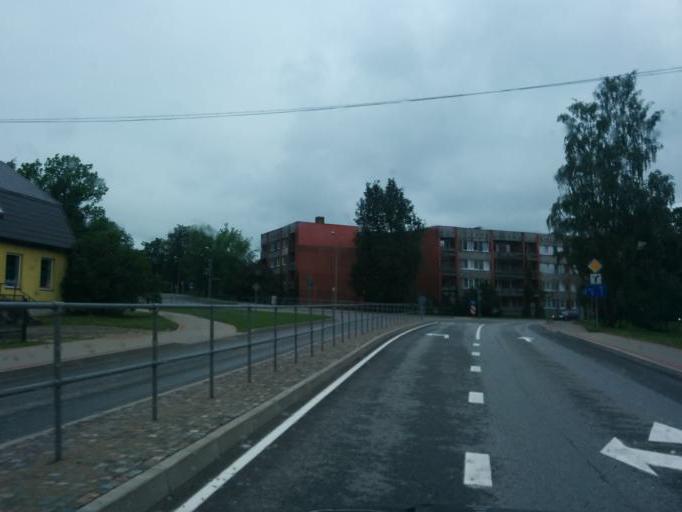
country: LV
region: Smiltene
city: Smiltene
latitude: 57.4252
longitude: 25.8997
